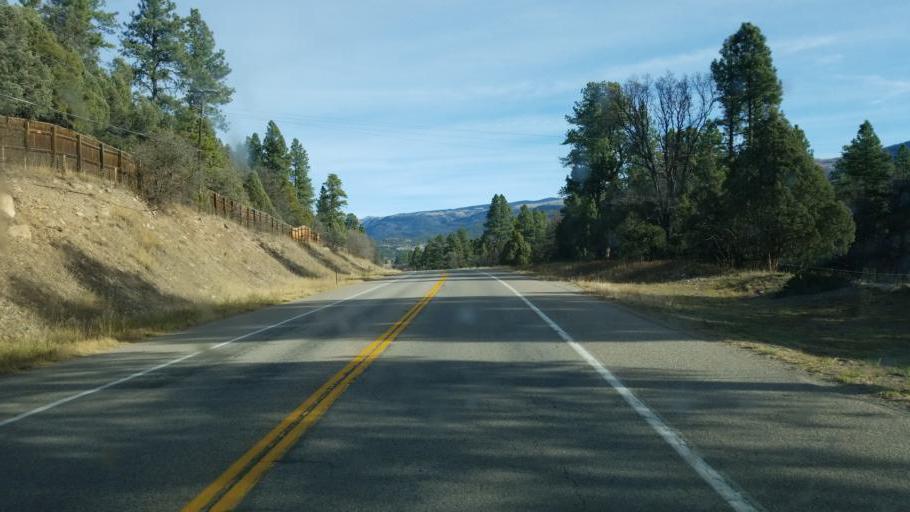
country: US
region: Colorado
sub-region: La Plata County
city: Durango
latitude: 37.4331
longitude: -107.8120
